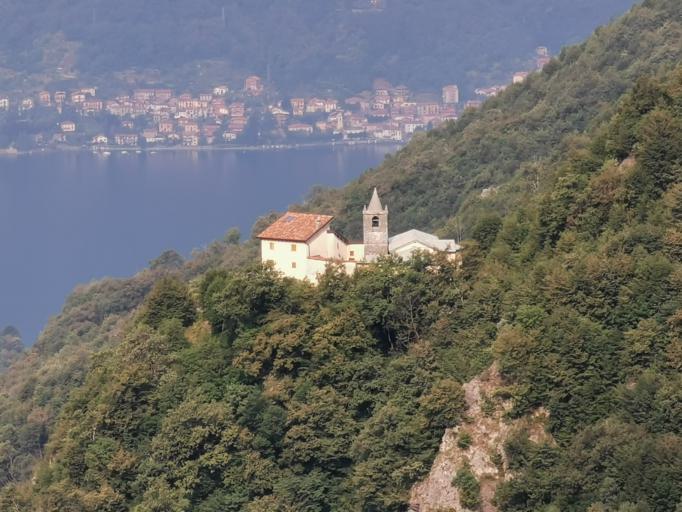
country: IT
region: Lombardy
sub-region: Provincia di Lecco
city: Mandello del Lario
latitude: 45.9355
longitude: 9.3527
